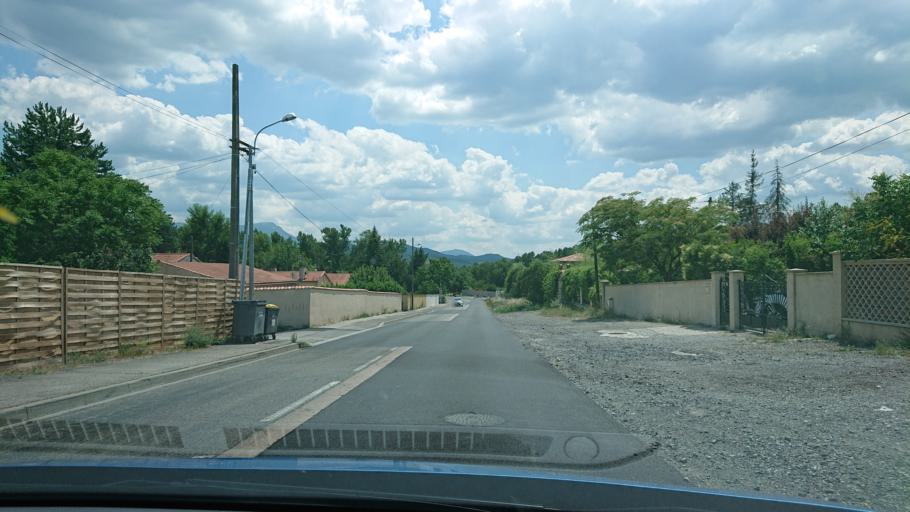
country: FR
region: Provence-Alpes-Cote d'Azur
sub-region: Departement des Alpes-de-Haute-Provence
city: Digne-les-Bains
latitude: 44.0772
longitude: 6.1755
